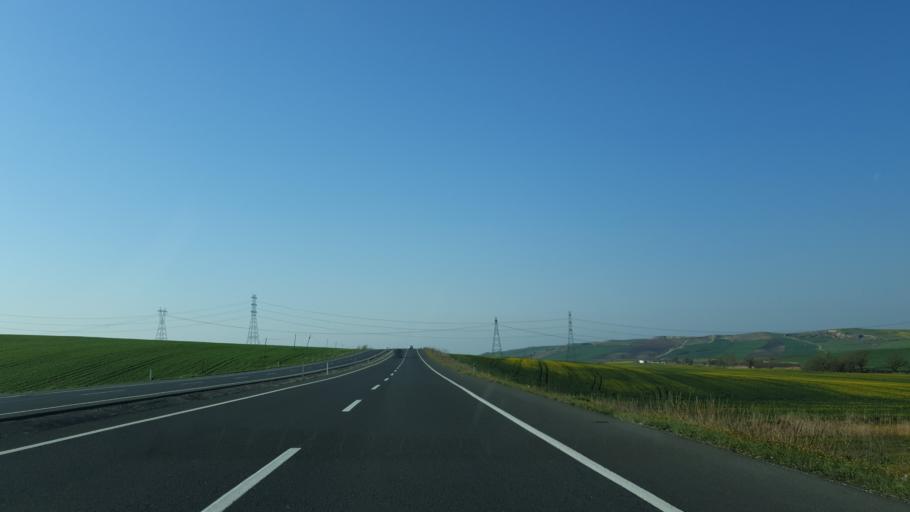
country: TR
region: Tekirdag
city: Corlu
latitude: 41.0780
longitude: 27.7415
